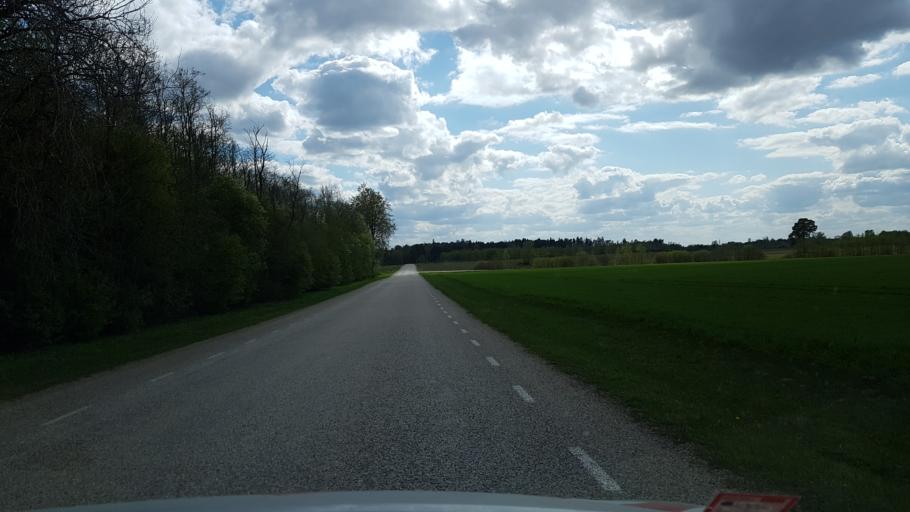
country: EE
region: Tartu
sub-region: Tartu linn
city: Tartu
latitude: 58.3522
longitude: 26.8517
